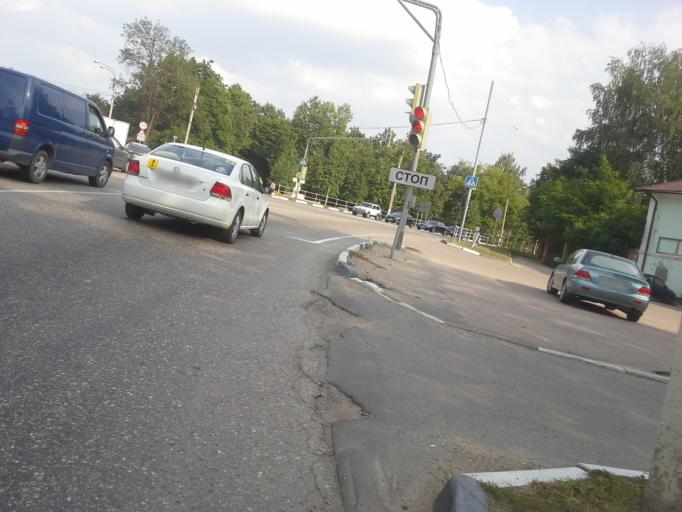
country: RU
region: Moskovskaya
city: Istra
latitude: 55.9205
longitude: 36.8574
